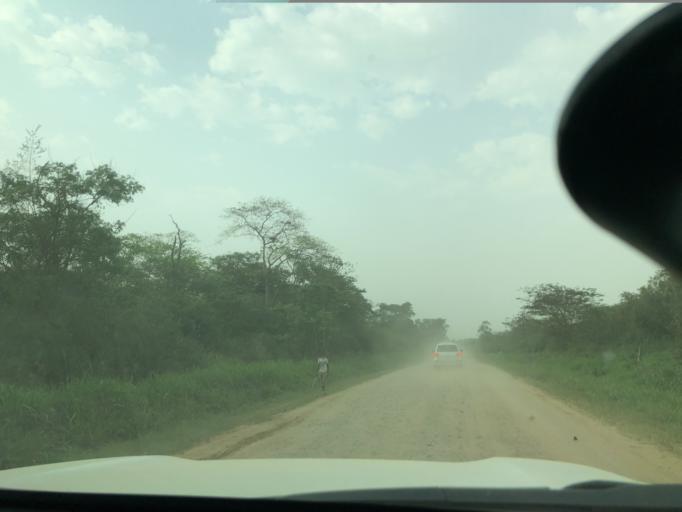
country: UG
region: Western Region
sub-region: Kasese District
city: Margherita
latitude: 0.2417
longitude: 29.6786
